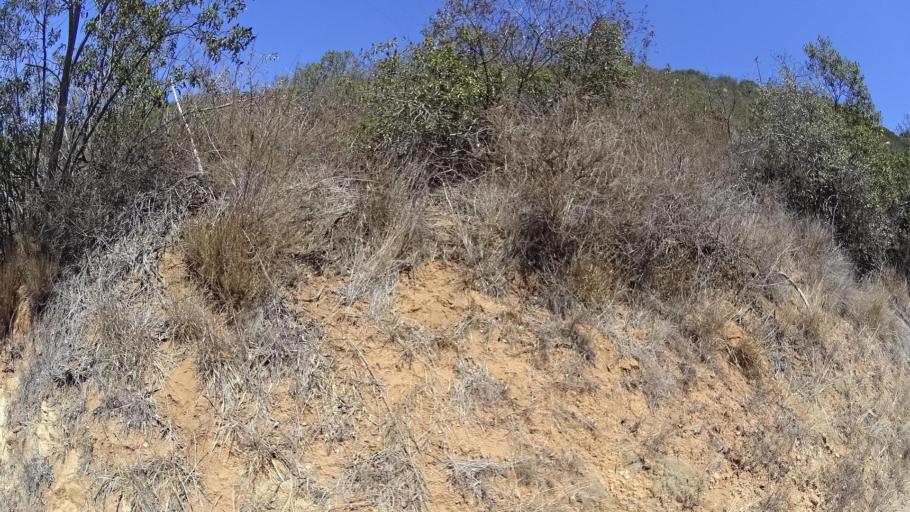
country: US
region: California
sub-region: San Diego County
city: Rainbow
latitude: 33.3879
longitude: -117.1035
